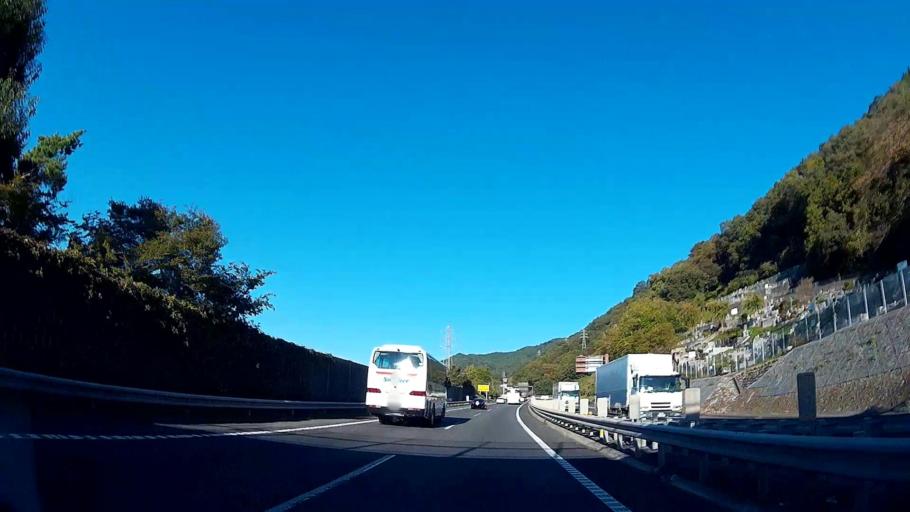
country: JP
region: Yamanashi
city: Uenohara
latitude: 35.6190
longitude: 139.1835
